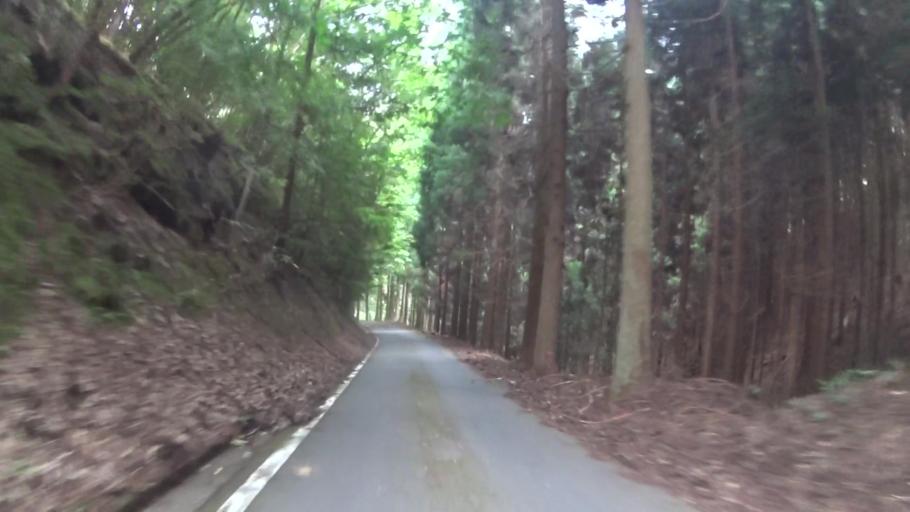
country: JP
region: Kyoto
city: Kameoka
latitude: 35.1678
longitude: 135.5746
